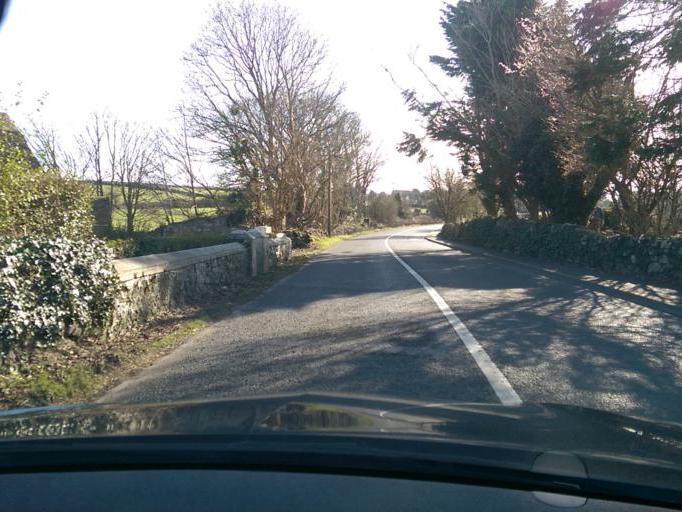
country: IE
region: Connaught
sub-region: County Galway
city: Oranmore
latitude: 53.2570
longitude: -8.9351
